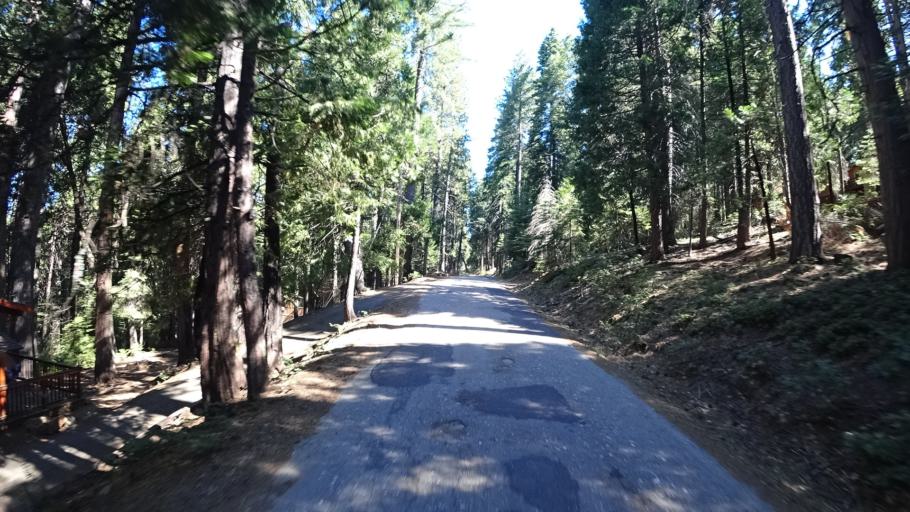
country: US
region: California
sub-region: Calaveras County
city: Arnold
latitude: 38.2972
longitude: -120.2717
